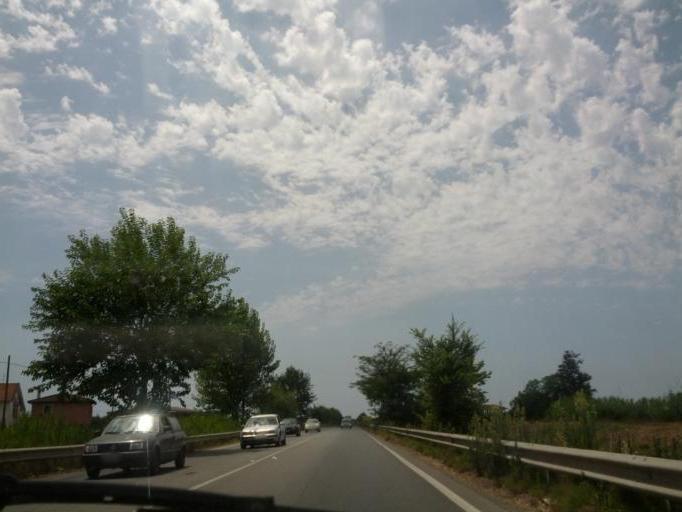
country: IT
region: Latium
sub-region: Provincia di Latina
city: Fondi
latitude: 41.3200
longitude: 13.4137
